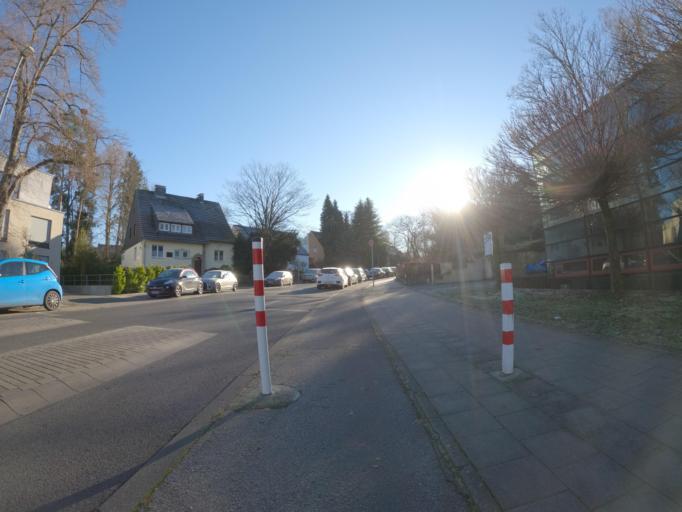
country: DE
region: North Rhine-Westphalia
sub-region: Regierungsbezirk Koln
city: Aachen
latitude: 50.7865
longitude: 6.0900
